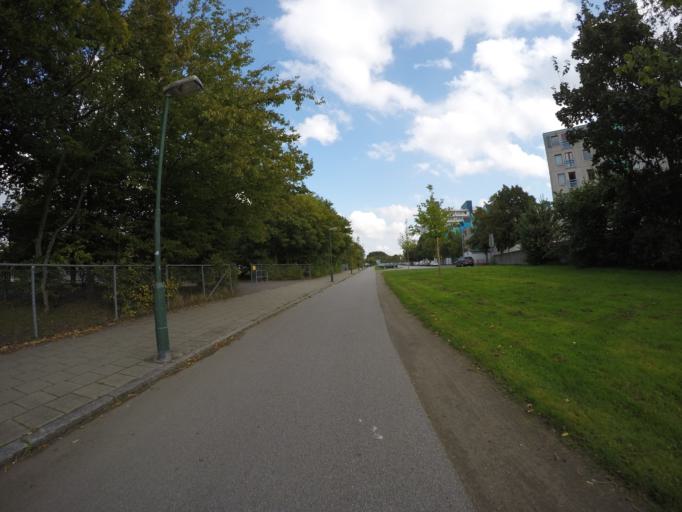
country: SE
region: Skane
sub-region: Burlovs Kommun
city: Arloev
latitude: 55.5884
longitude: 13.0514
